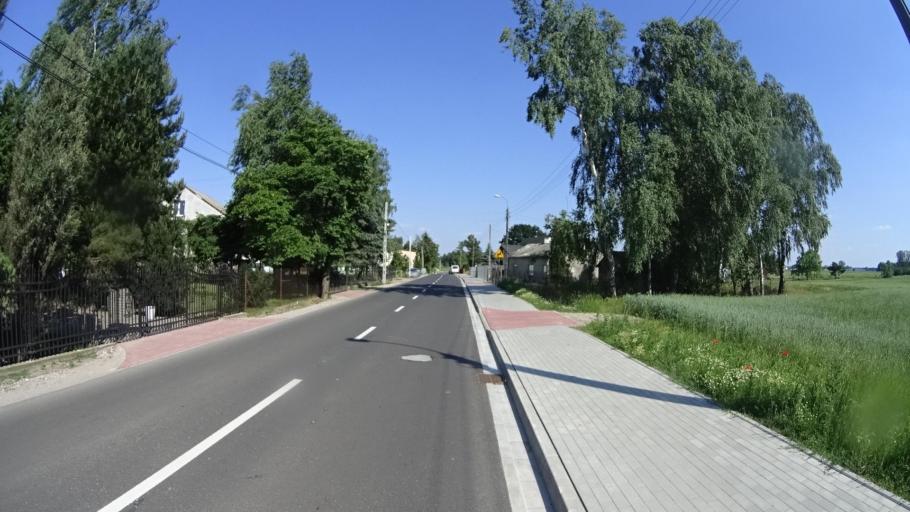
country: PL
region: Masovian Voivodeship
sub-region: Powiat warszawski zachodni
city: Blonie
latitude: 52.1663
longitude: 20.6268
